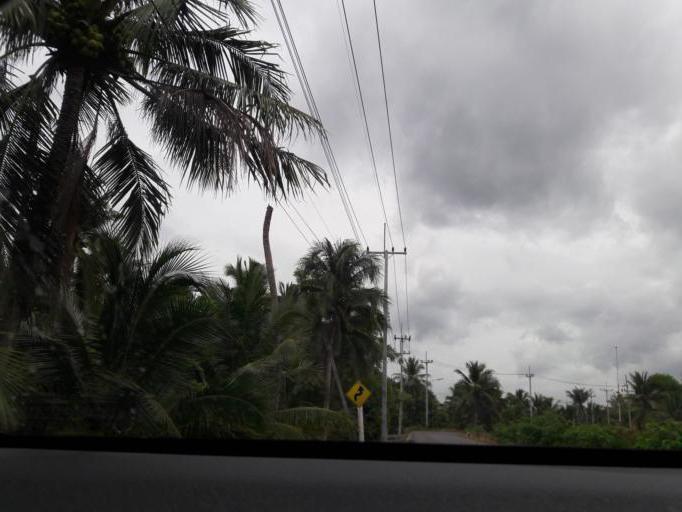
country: TH
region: Ratchaburi
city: Damnoen Saduak
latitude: 13.5746
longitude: 99.9991
